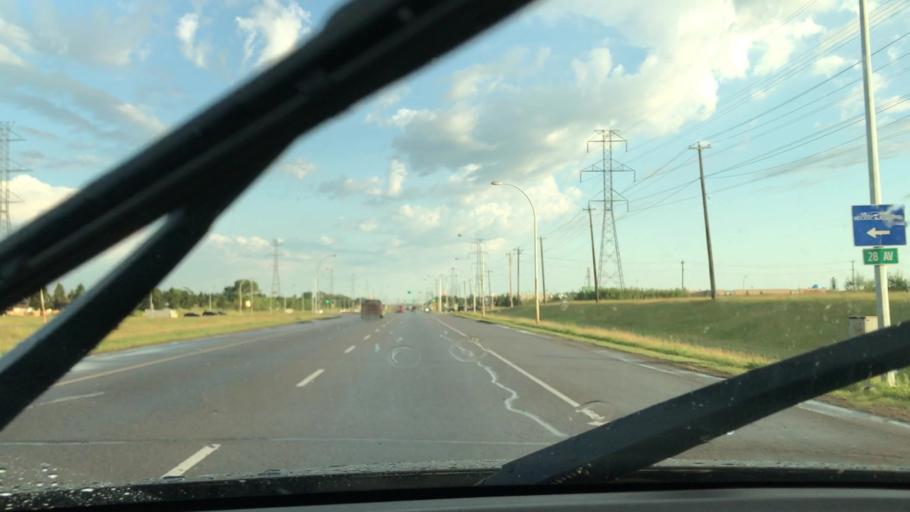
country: CA
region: Alberta
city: Edmonton
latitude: 53.4610
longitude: -113.4669
